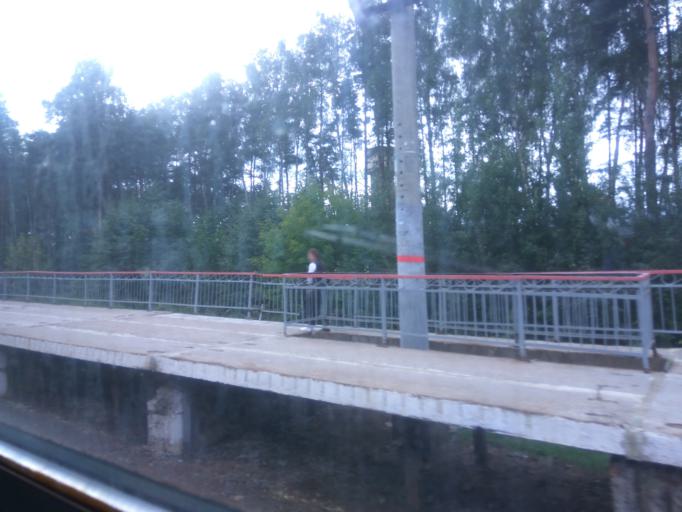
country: RU
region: Moskovskaya
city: Beloozerskiy
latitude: 55.4619
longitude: 38.4498
